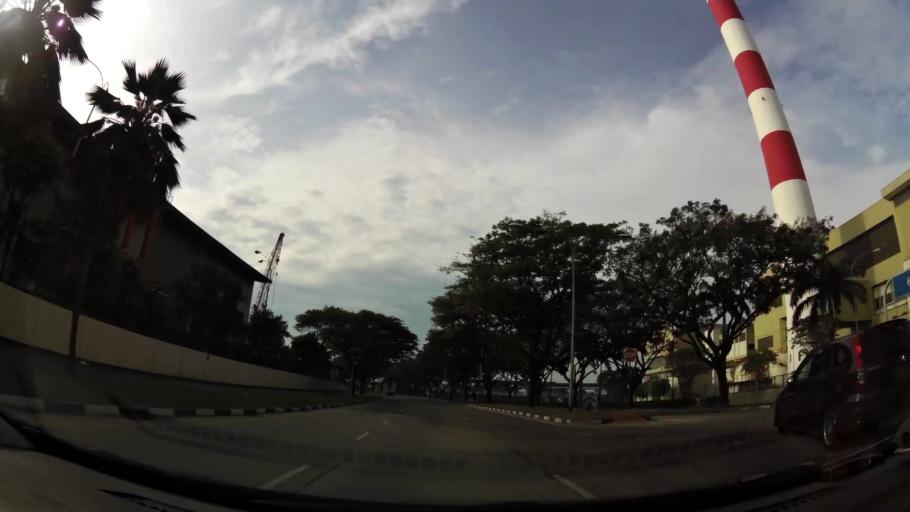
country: MY
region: Johor
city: Johor Bahru
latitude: 1.2960
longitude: 103.6221
